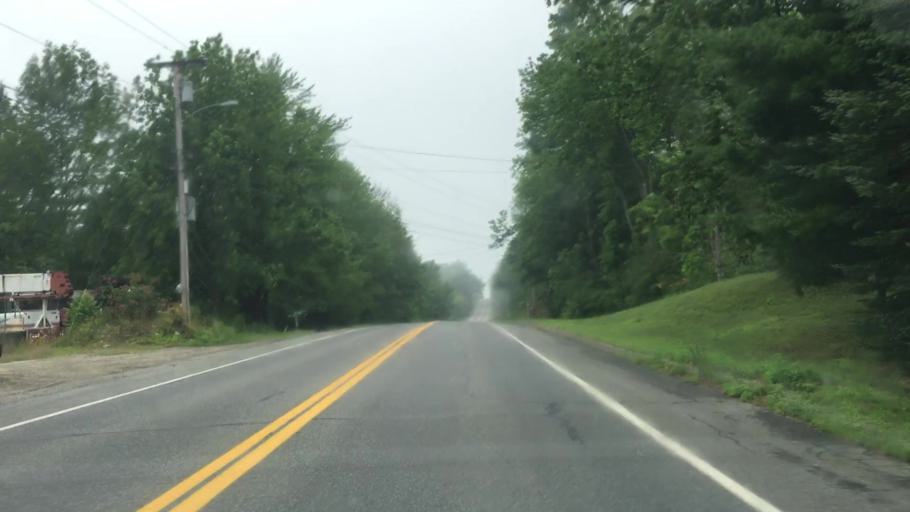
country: US
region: Maine
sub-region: Lincoln County
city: Wiscasset
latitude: 44.0599
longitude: -69.6873
